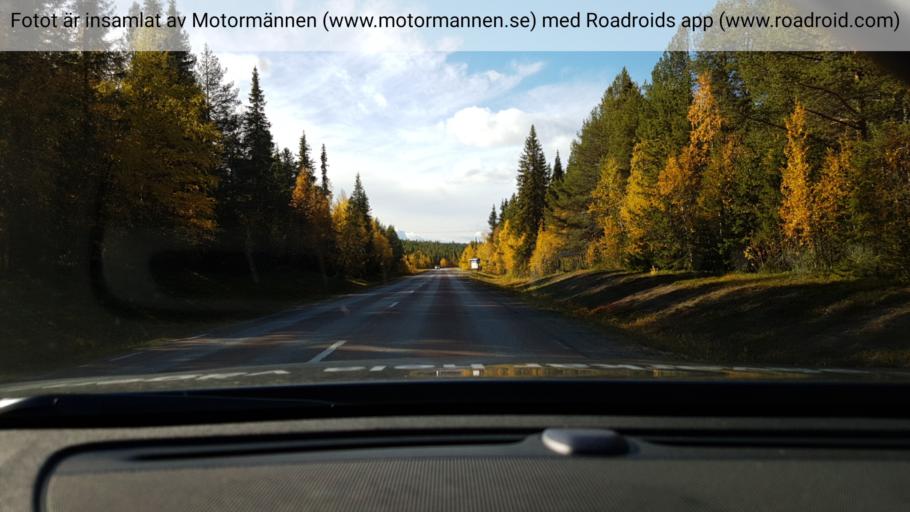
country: SE
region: Norrbotten
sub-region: Arjeplogs Kommun
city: Arjeplog
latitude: 66.0572
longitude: 17.9333
